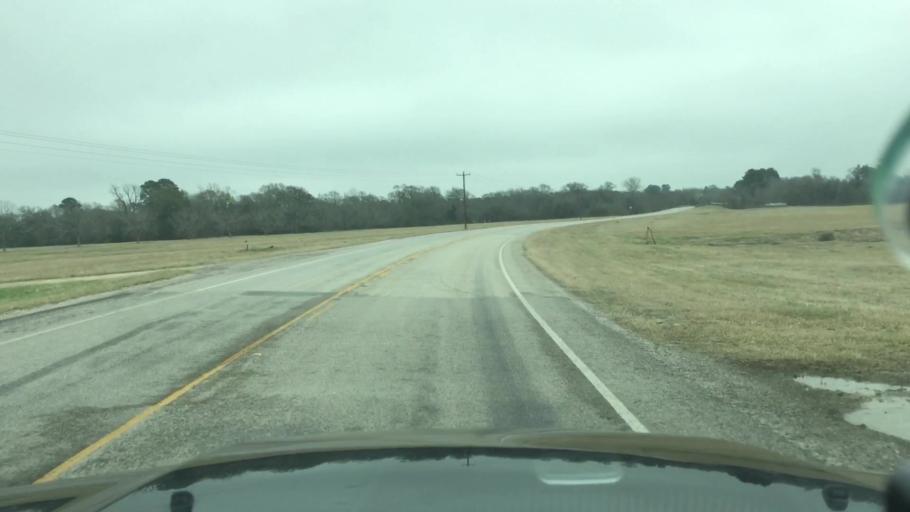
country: US
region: Texas
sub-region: Fayette County
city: La Grange
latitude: 30.0111
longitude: -96.9140
